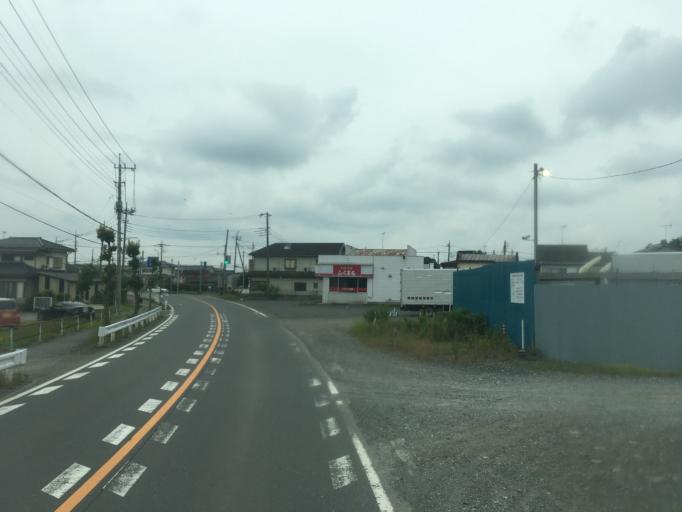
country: JP
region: Saitama
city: Kawagoe
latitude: 35.9709
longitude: 139.4628
